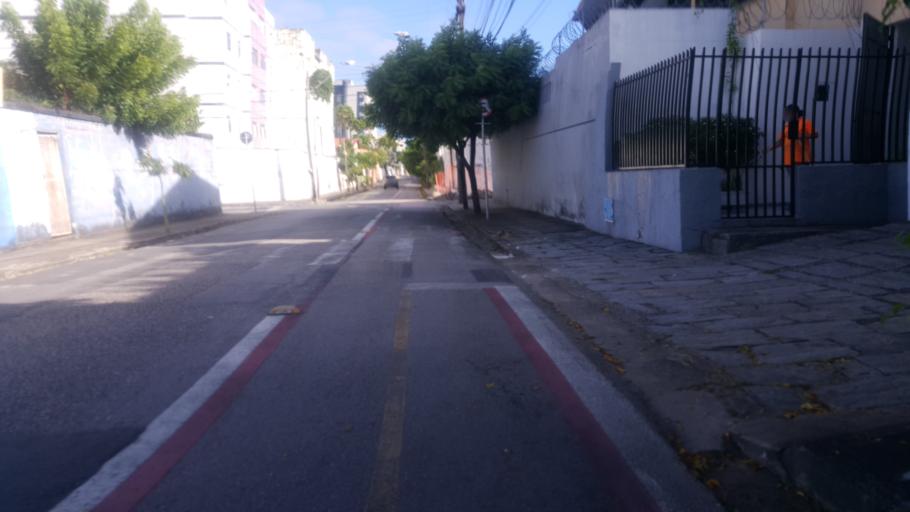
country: BR
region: Ceara
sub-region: Fortaleza
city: Fortaleza
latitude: -3.7474
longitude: -38.5387
